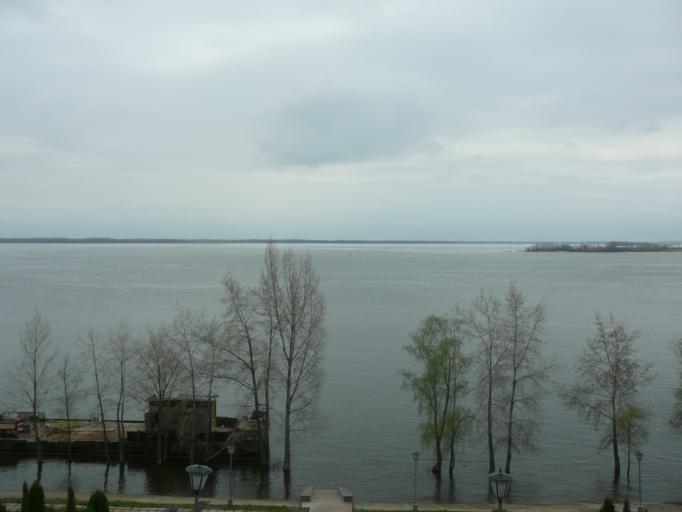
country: RU
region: Saratov
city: Shumeyka
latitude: 51.5942
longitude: 46.1862
